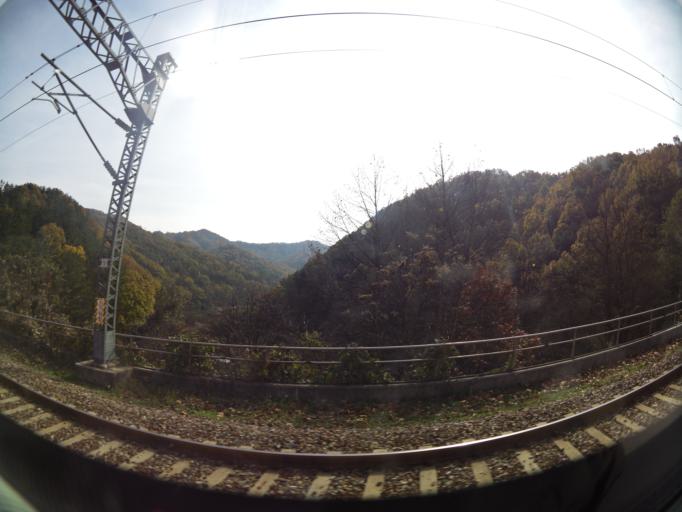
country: KR
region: Daejeon
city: Daejeon
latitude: 36.3361
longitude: 127.4900
